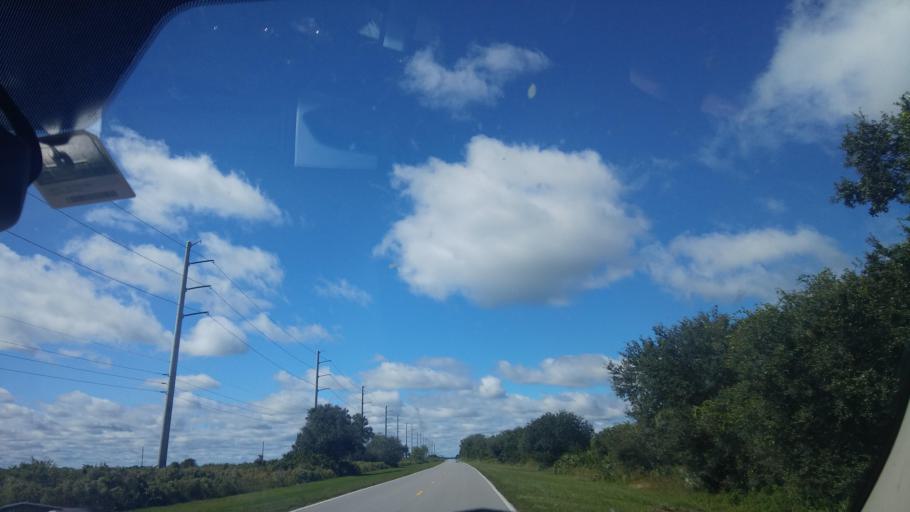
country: US
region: Florida
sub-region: Okeechobee County
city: Cypress Quarters
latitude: 27.4494
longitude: -80.7805
